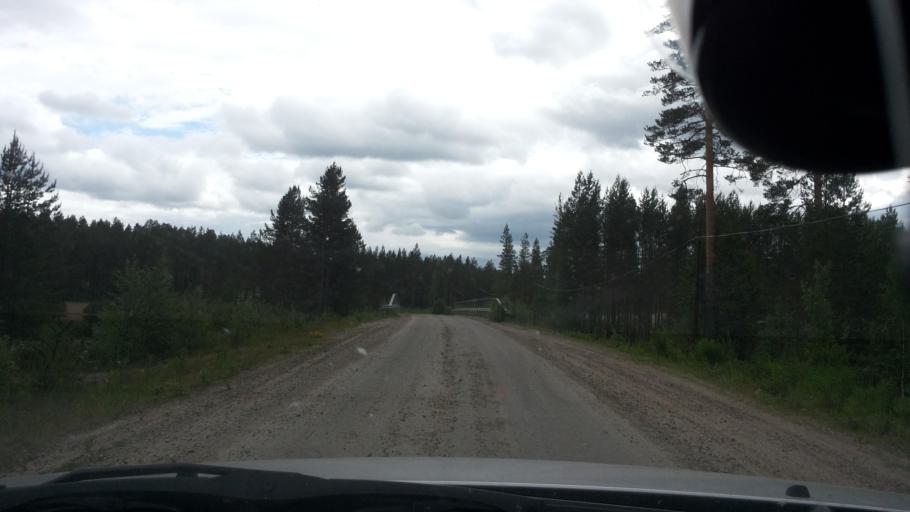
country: SE
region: Gaevleborg
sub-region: Ovanakers Kommun
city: Edsbyn
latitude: 61.5039
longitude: 15.3391
